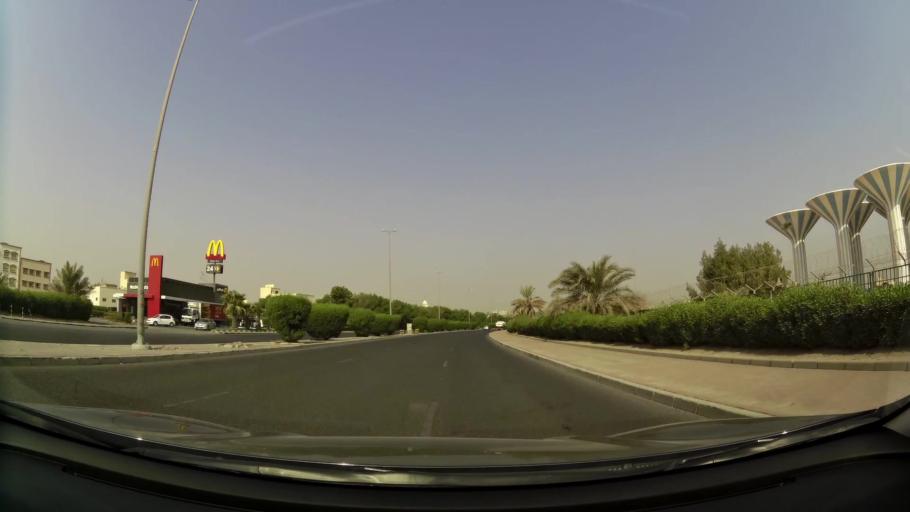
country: KW
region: Al Asimah
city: Ar Rabiyah
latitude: 29.2876
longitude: 47.8811
